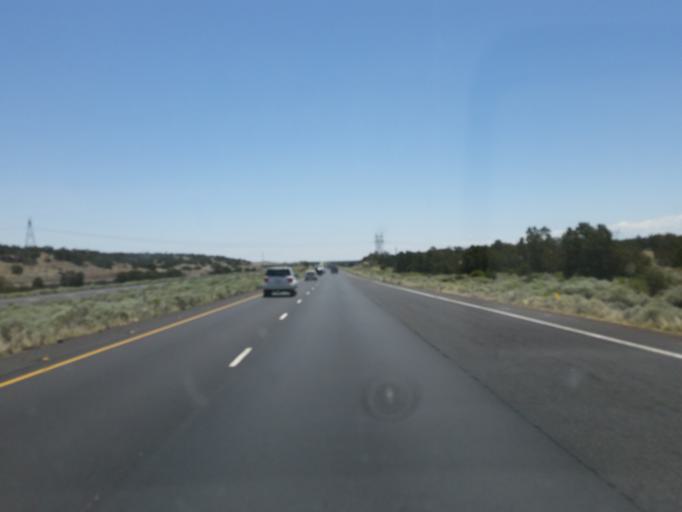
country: US
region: Arizona
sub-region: Coconino County
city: Flagstaff
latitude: 35.1990
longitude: -111.4007
